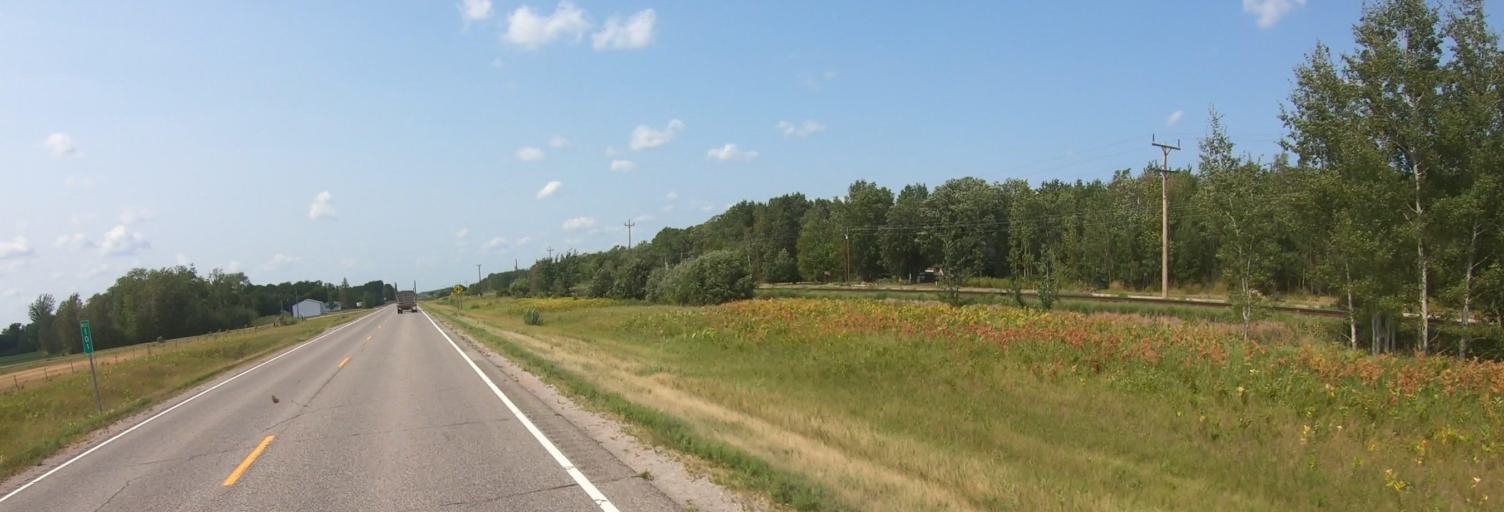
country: US
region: Minnesota
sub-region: Roseau County
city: Warroad
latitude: 48.8345
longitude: -95.1760
